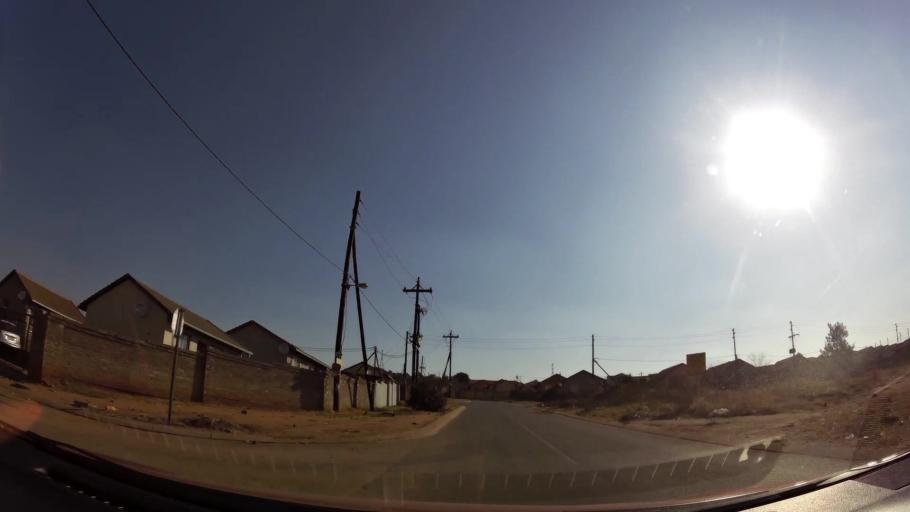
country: ZA
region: Gauteng
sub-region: West Rand District Municipality
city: Muldersdriseloop
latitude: -26.0316
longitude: 27.9182
